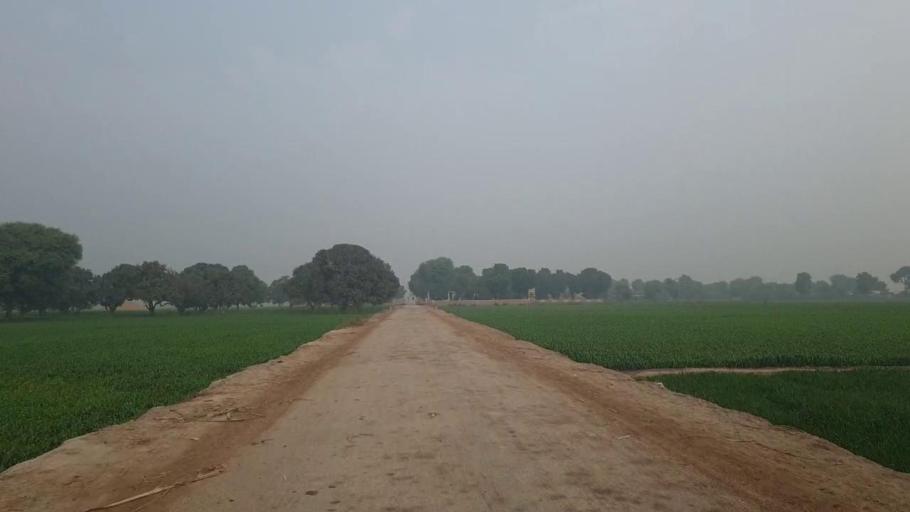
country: PK
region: Sindh
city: Tando Adam
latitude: 25.7105
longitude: 68.6594
